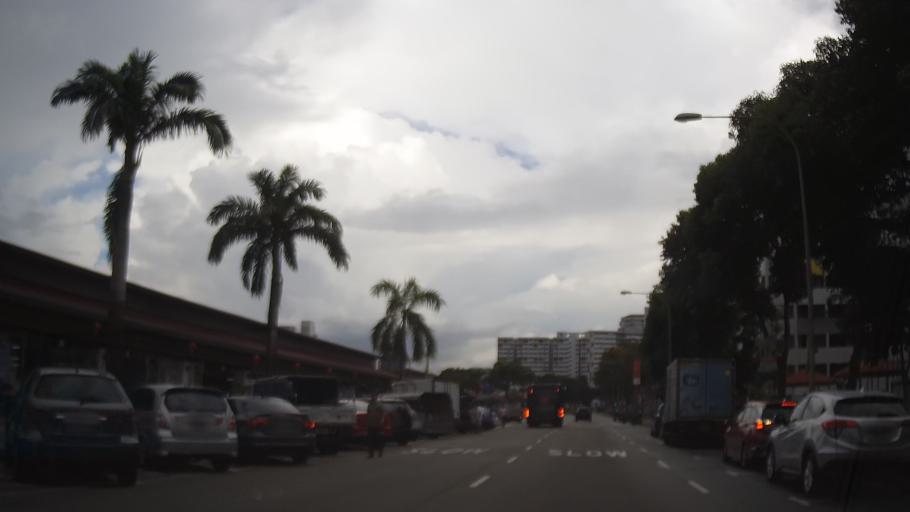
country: SG
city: Singapore
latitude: 1.3253
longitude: 103.8851
